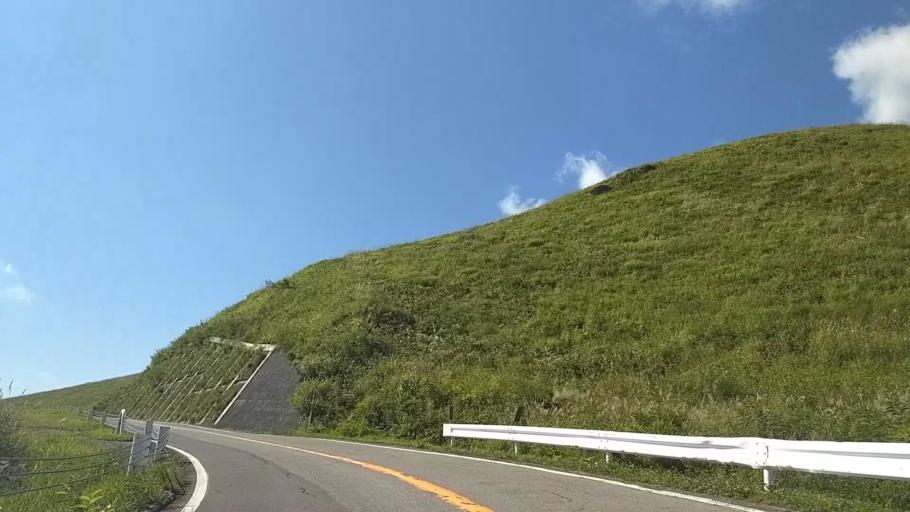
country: JP
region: Nagano
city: Suwa
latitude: 36.1013
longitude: 138.2181
